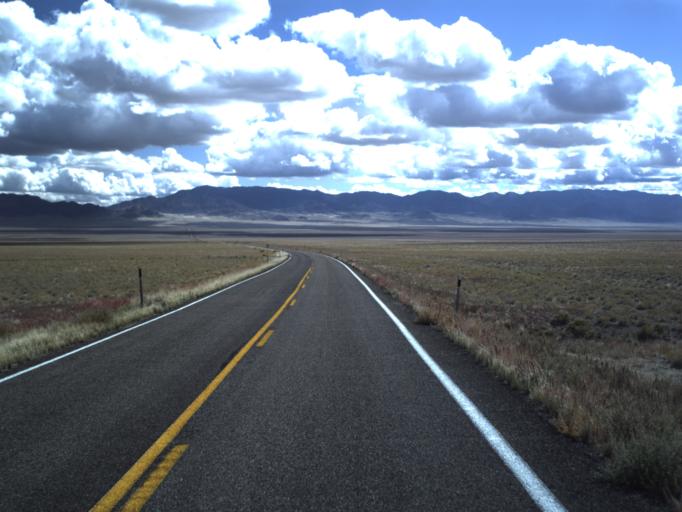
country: US
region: Utah
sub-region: Beaver County
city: Milford
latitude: 38.5776
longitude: -113.8032
